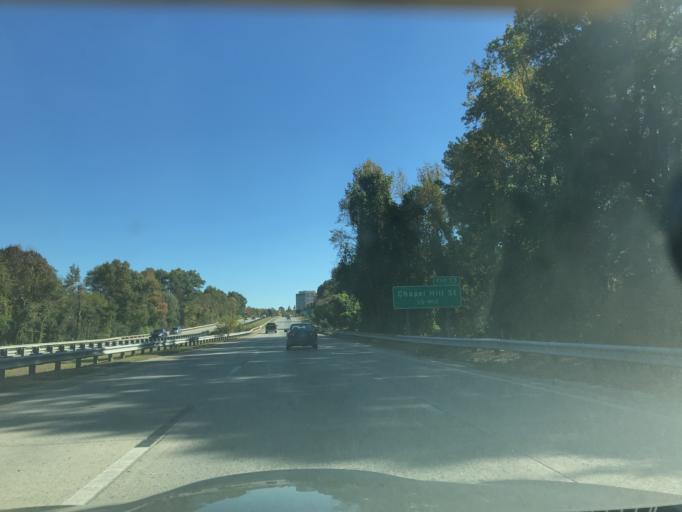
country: US
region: North Carolina
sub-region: Durham County
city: Durham
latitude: 36.0030
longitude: -78.9194
